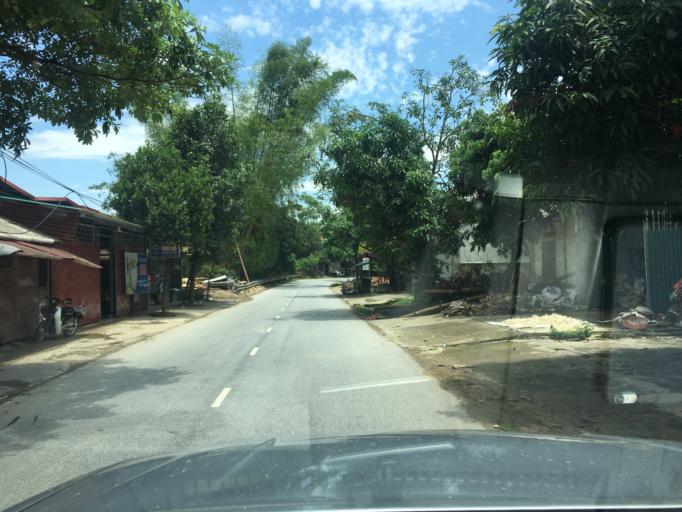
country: VN
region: Yen Bai
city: Son Thinh
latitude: 21.6516
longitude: 104.5009
